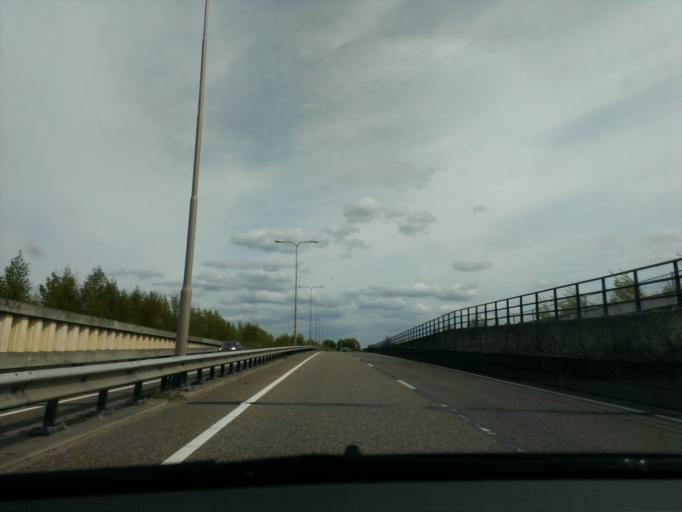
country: NL
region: Gelderland
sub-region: Gemeente Harderwijk
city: Harderwijk
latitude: 52.3600
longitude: 5.6205
